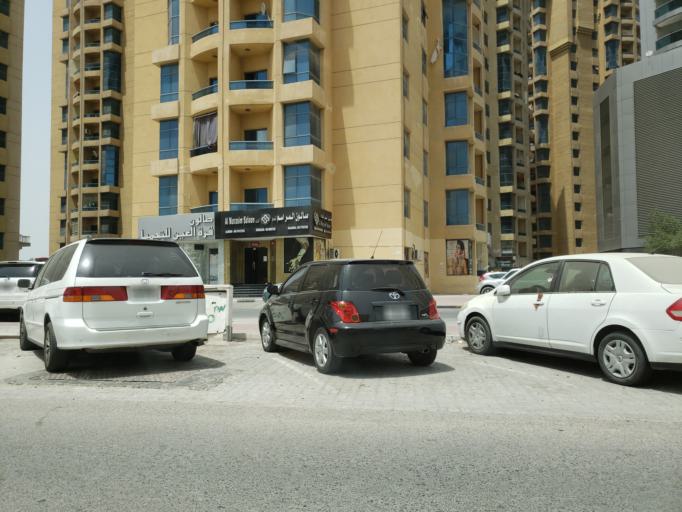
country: AE
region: Ajman
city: Ajman
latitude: 25.3935
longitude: 55.4568
